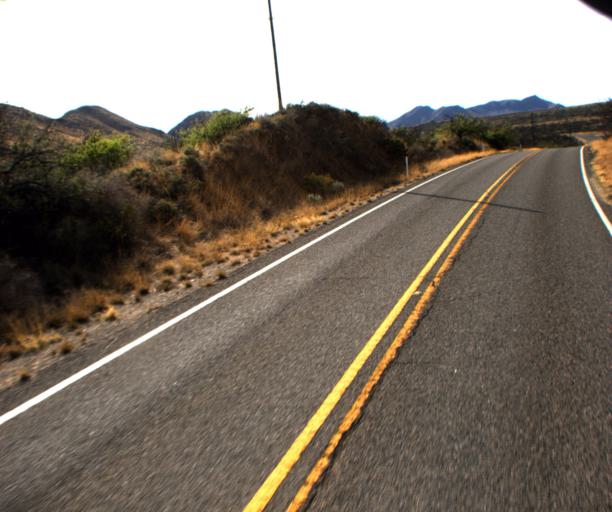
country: US
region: Arizona
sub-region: Cochise County
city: Willcox
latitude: 32.1723
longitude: -109.6008
